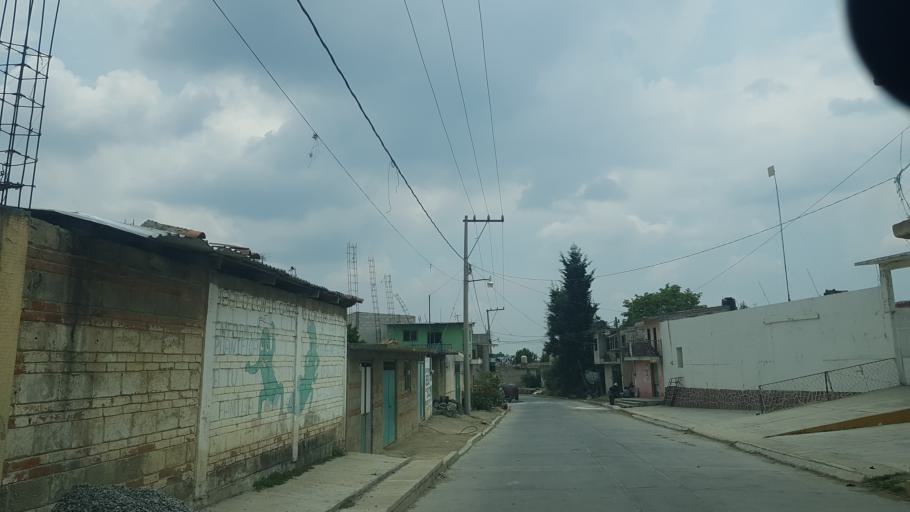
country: MX
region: Puebla
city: Domingo Arenas
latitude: 19.1513
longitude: -98.4977
